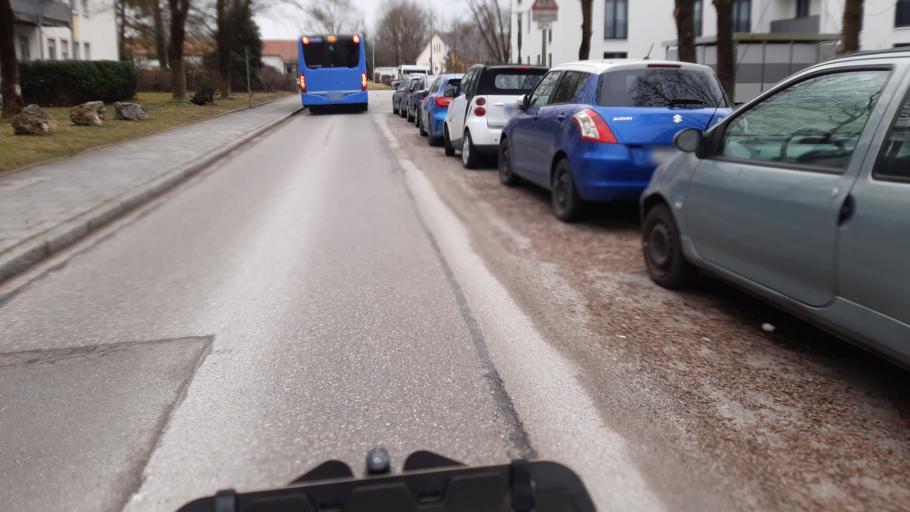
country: DE
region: Bavaria
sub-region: Upper Bavaria
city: Karlsfeld
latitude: 48.2145
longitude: 11.4868
